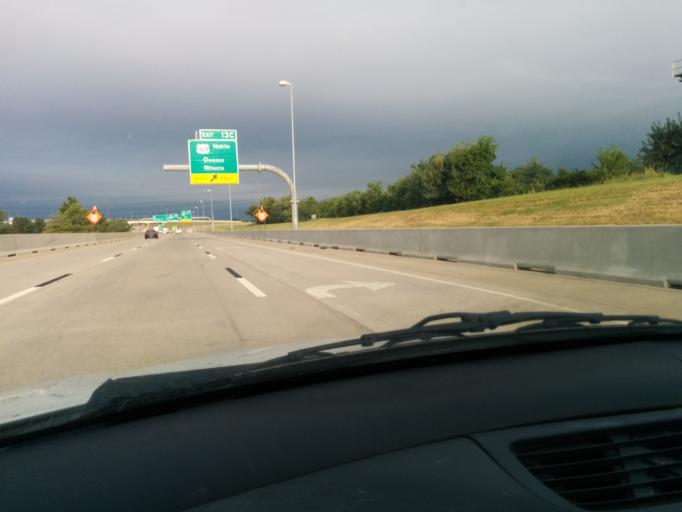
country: US
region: Oklahoma
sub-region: Tulsa County
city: Owasso
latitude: 36.1663
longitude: -95.8529
